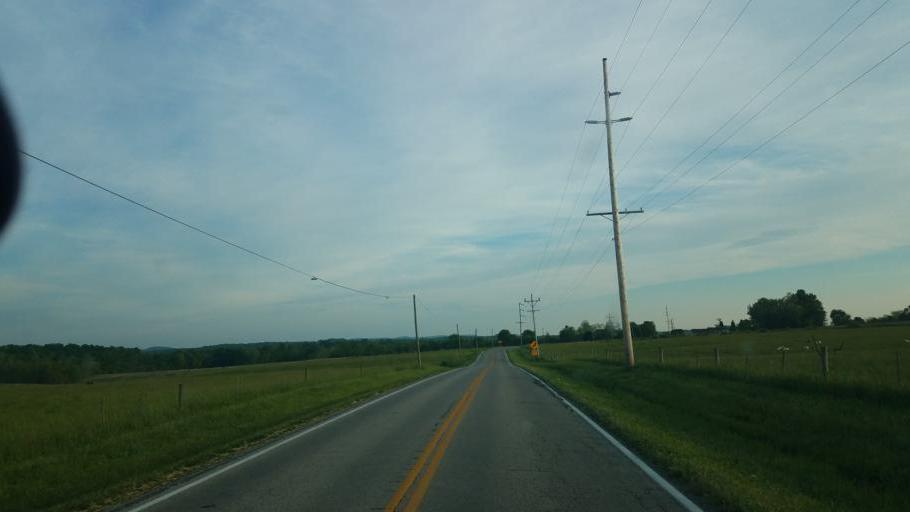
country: US
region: Ohio
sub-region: Highland County
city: Greenfield
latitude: 39.2941
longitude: -83.4098
